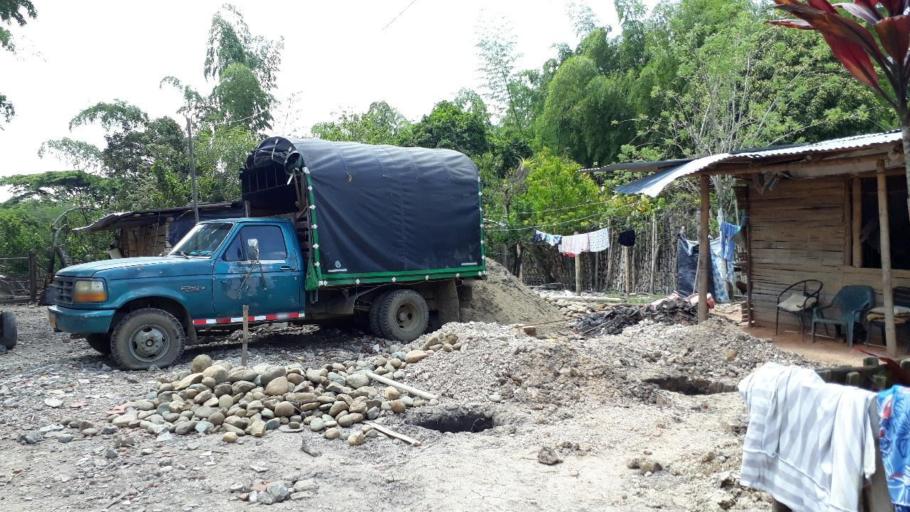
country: CO
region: Valle del Cauca
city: Jamundi
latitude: 3.1369
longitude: -76.5433
